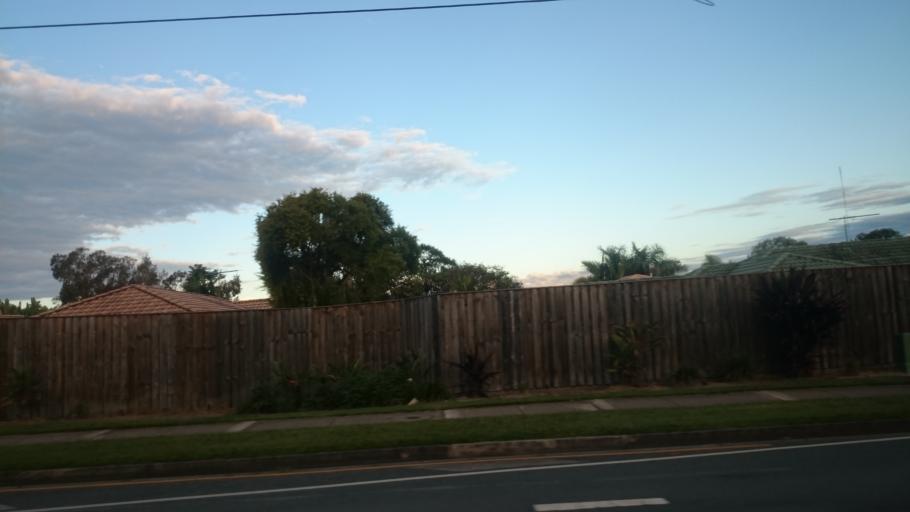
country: AU
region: Queensland
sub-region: Brisbane
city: Wynnum West
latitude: -27.4611
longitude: 153.1485
